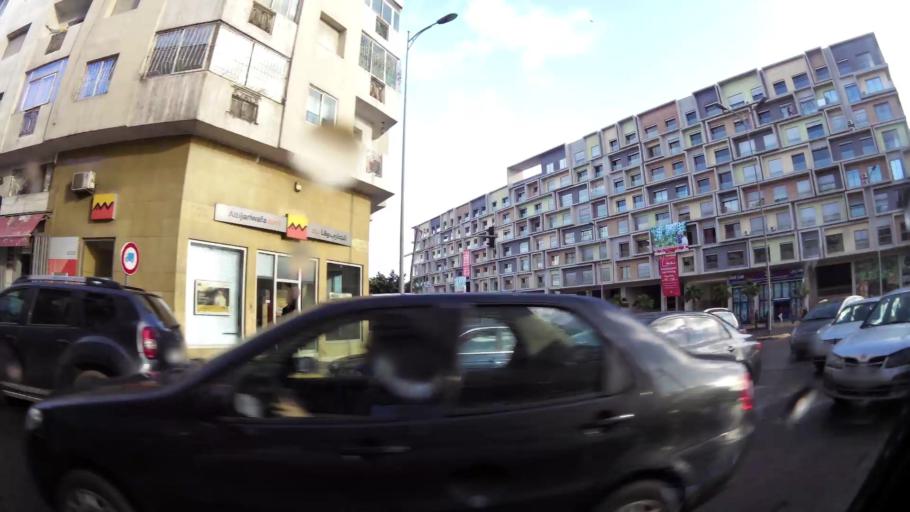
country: MA
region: Grand Casablanca
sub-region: Casablanca
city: Casablanca
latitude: 33.5845
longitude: -7.5980
